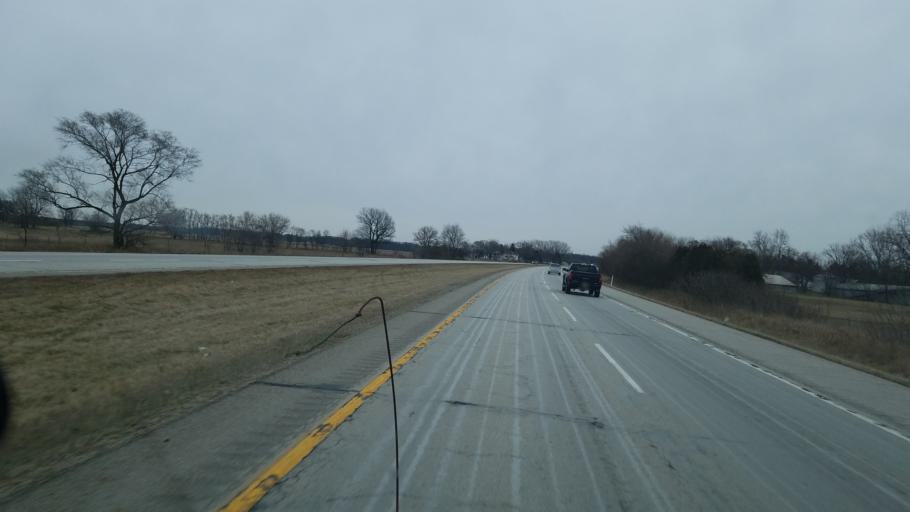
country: US
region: Indiana
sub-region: Starke County
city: Knox
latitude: 41.3923
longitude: -86.5906
